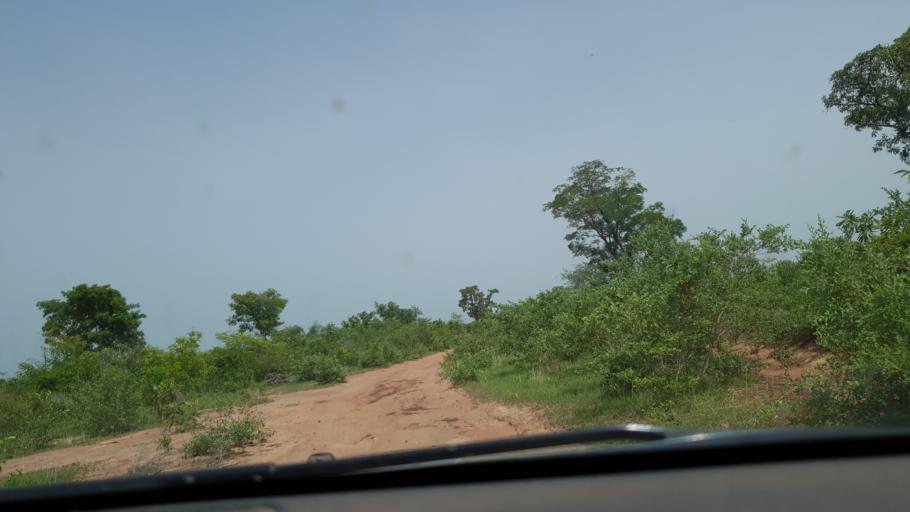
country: ML
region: Koulikoro
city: Koulikoro
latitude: 12.6650
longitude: -7.2215
